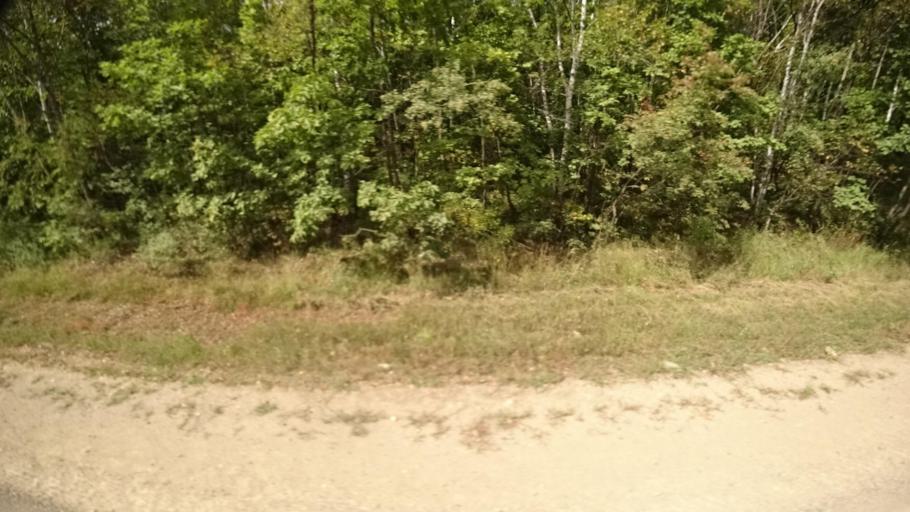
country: RU
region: Primorskiy
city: Yakovlevka
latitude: 44.6603
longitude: 133.5982
